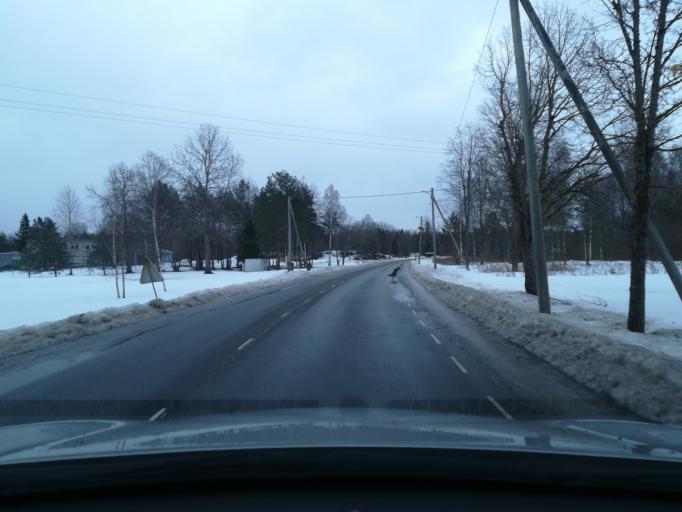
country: EE
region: Harju
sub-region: Nissi vald
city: Turba
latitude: 59.0737
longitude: 24.2449
